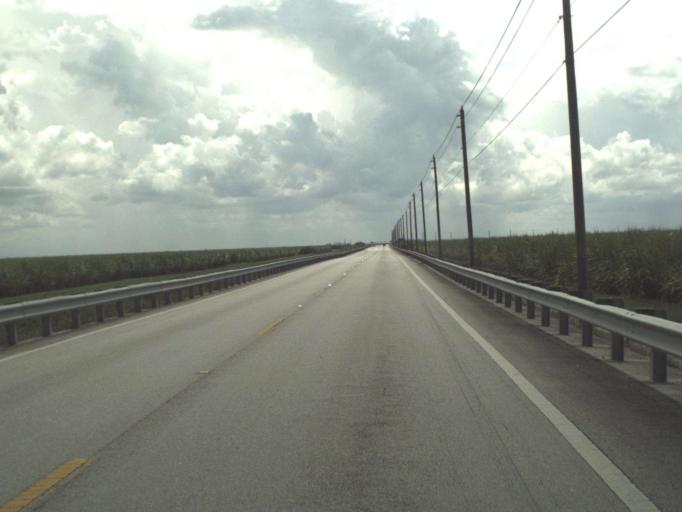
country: US
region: Florida
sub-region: Palm Beach County
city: Pahokee
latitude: 26.7798
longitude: -80.6534
